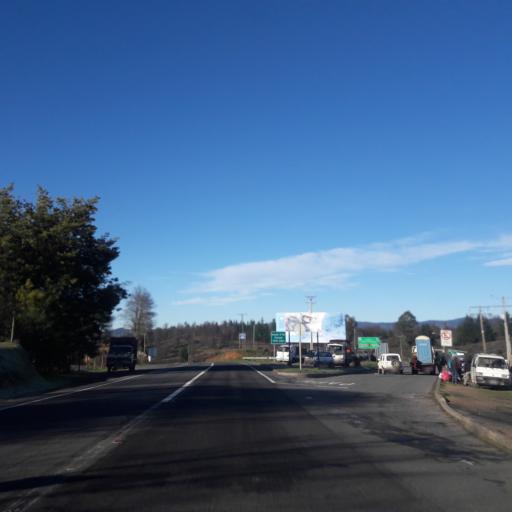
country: CL
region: Biobio
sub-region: Provincia de Biobio
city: La Laja
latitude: -37.3167
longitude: -72.9220
